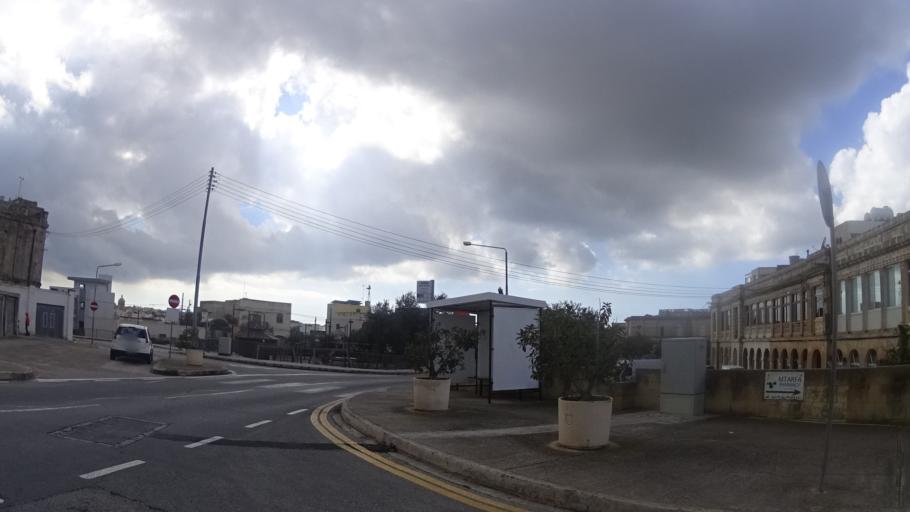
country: MT
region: L-Imtarfa
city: Imtarfa
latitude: 35.8913
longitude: 14.3980
